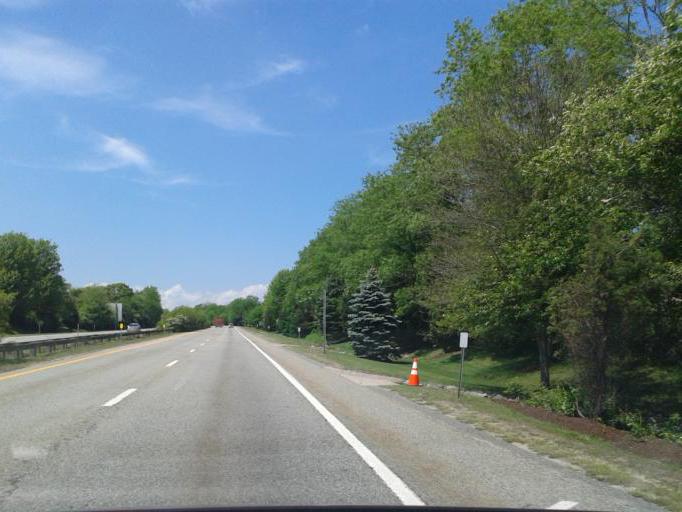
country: US
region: Rhode Island
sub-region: Newport County
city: Jamestown
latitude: 41.5205
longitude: -71.3665
